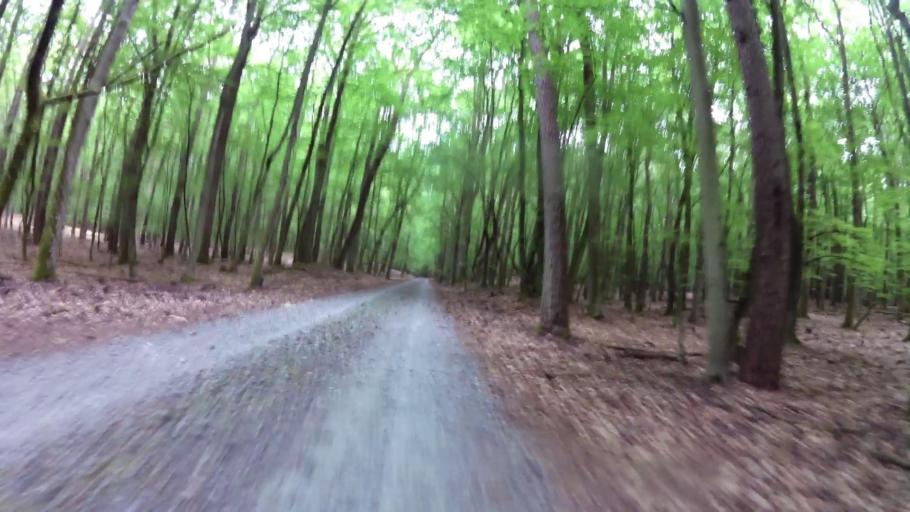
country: PL
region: West Pomeranian Voivodeship
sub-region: Powiat kamienski
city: Miedzyzdroje
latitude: 53.9495
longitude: 14.5441
